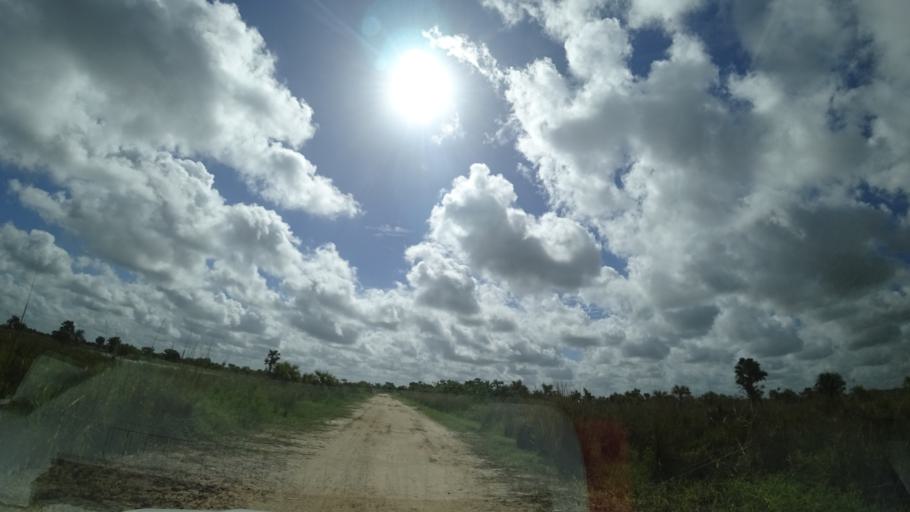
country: MZ
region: Sofala
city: Dondo
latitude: -19.3898
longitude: 34.5780
